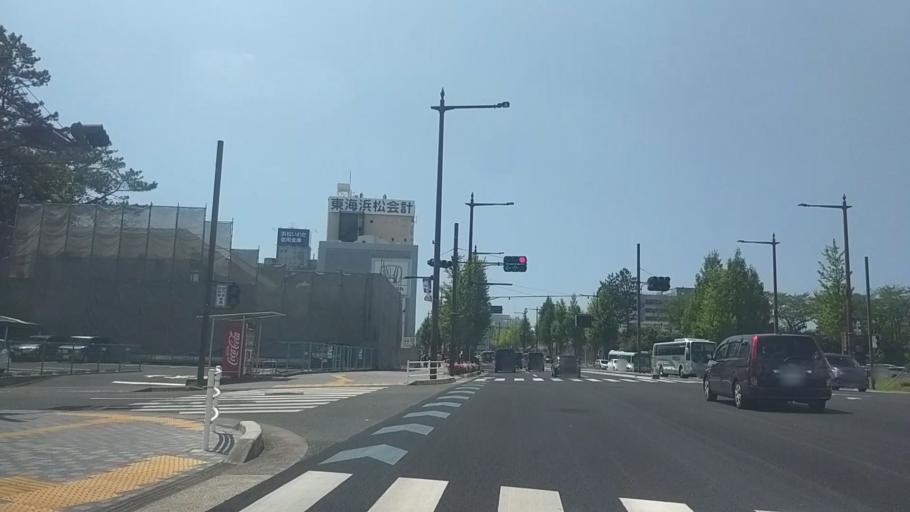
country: JP
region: Shizuoka
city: Hamamatsu
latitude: 34.7138
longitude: 137.7283
